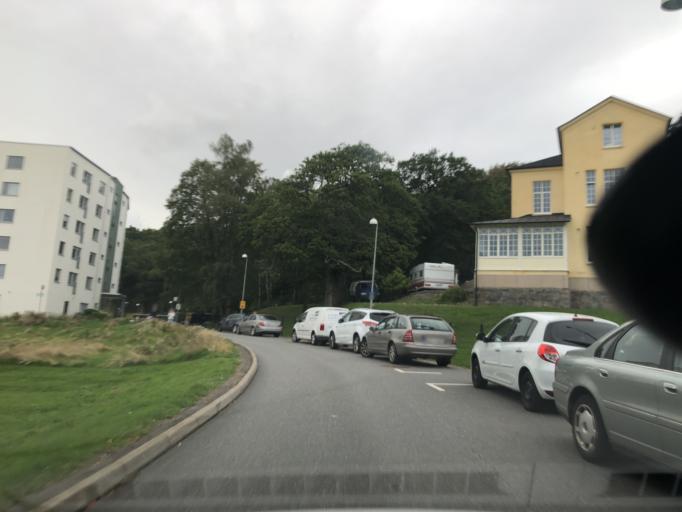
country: SE
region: Vaestra Goetaland
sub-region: Goteborg
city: Goeteborg
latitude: 57.7505
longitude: 11.9536
